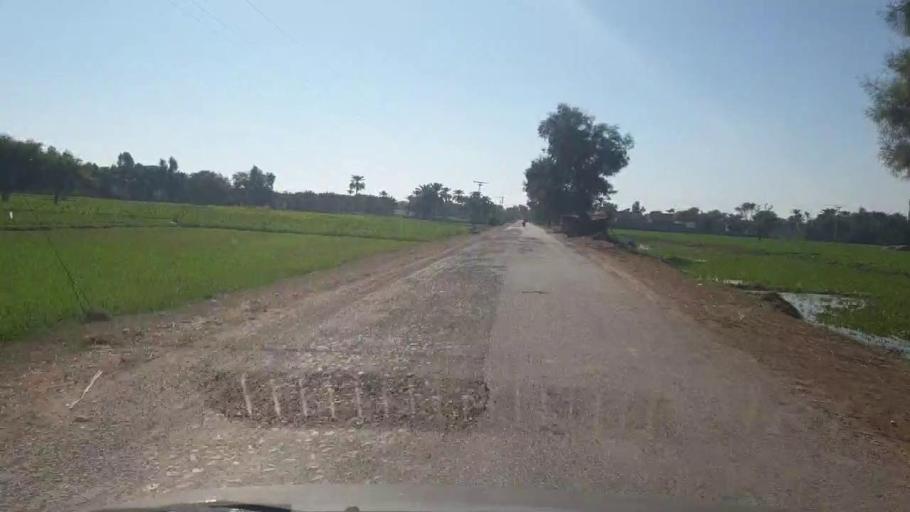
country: PK
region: Sindh
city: Bozdar
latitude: 27.1099
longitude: 68.6337
